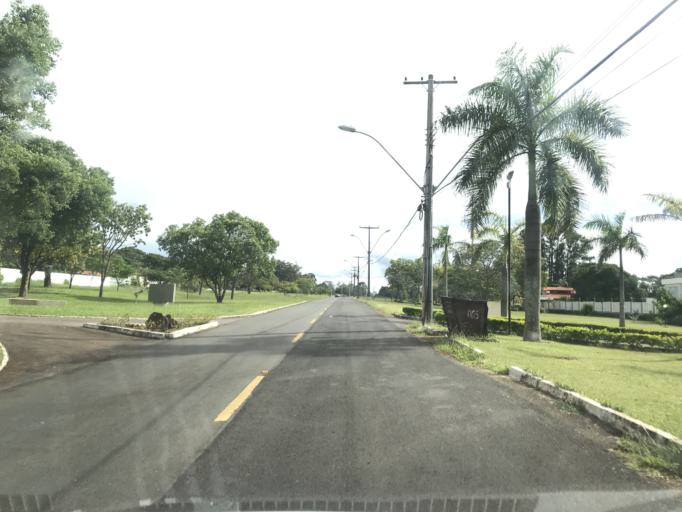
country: BR
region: Federal District
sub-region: Brasilia
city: Brasilia
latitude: -15.8964
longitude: -47.9195
